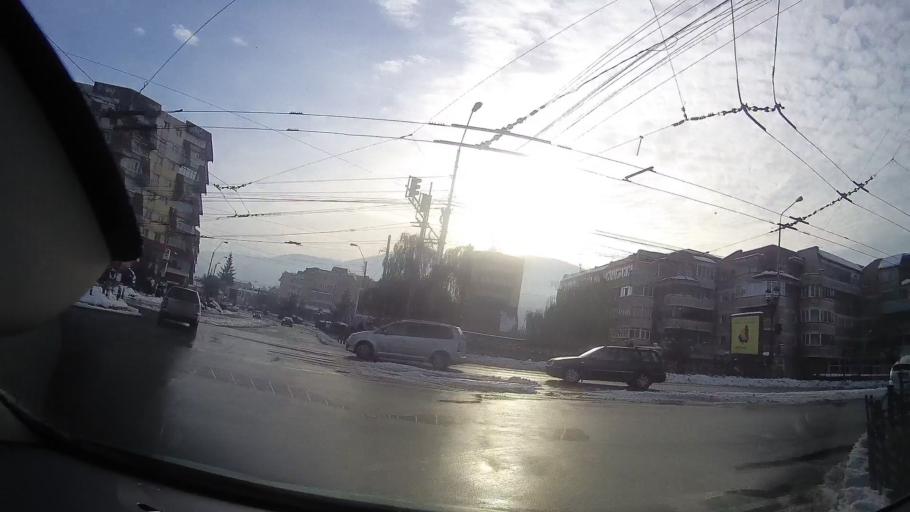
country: RO
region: Neamt
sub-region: Municipiul Piatra-Neamt
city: Valeni
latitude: 46.9269
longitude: 26.3721
